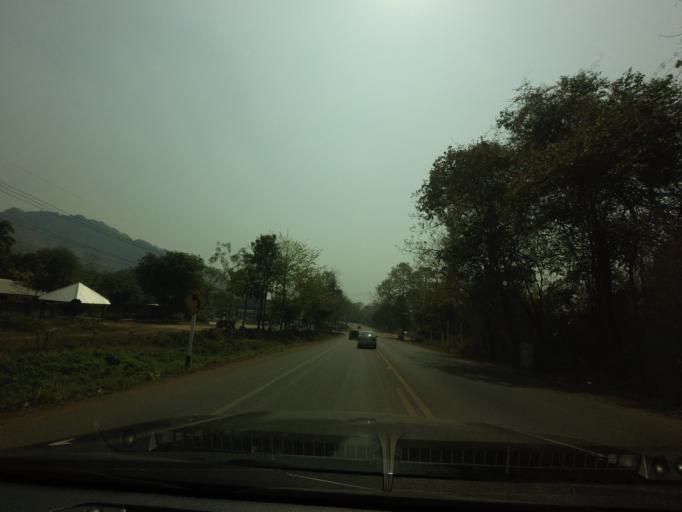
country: TH
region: Kanchanaburi
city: Thong Pha Phum
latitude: 14.7350
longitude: 98.6479
